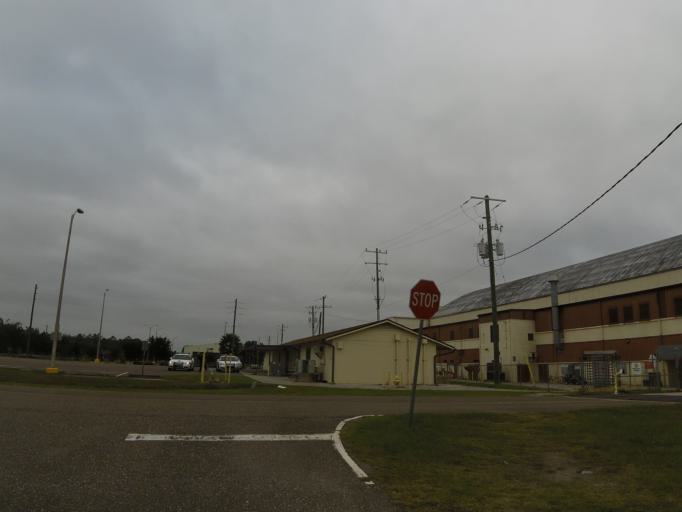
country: US
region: Florida
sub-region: Duval County
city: Baldwin
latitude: 30.2255
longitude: -81.8826
